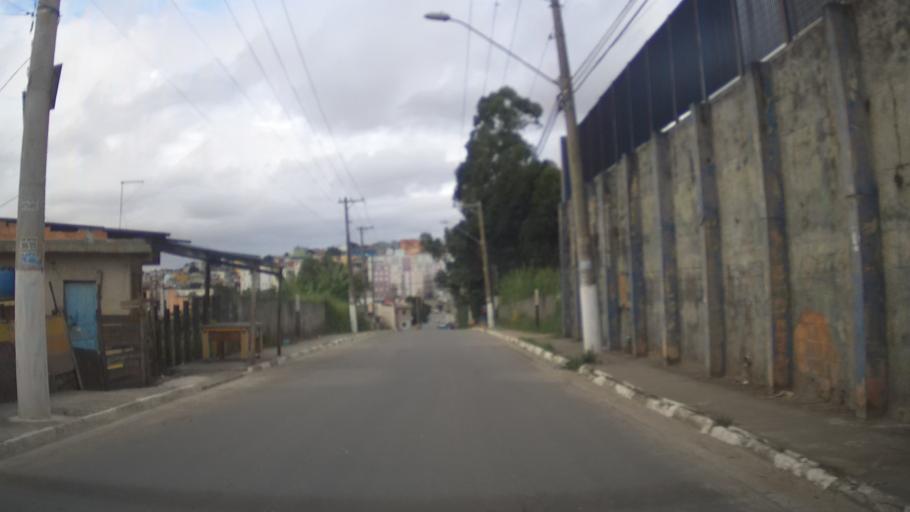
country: BR
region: Sao Paulo
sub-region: Itaquaquecetuba
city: Itaquaquecetuba
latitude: -23.4604
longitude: -46.3939
